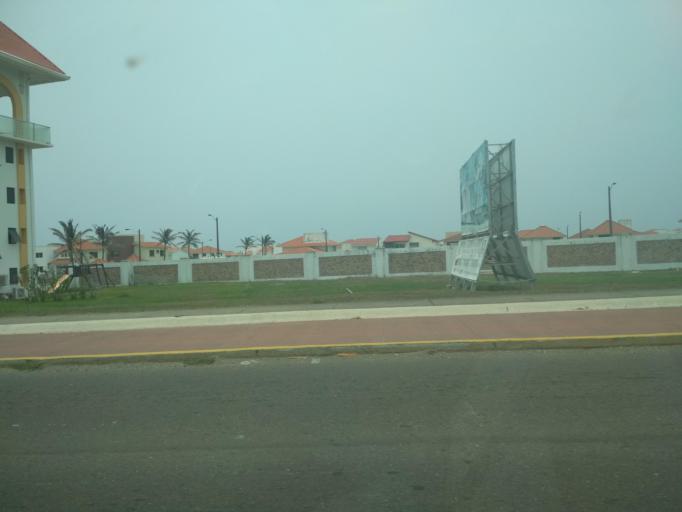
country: MX
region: Veracruz
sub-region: Alvarado
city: Playa de la Libertad
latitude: 19.0684
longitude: -96.0817
